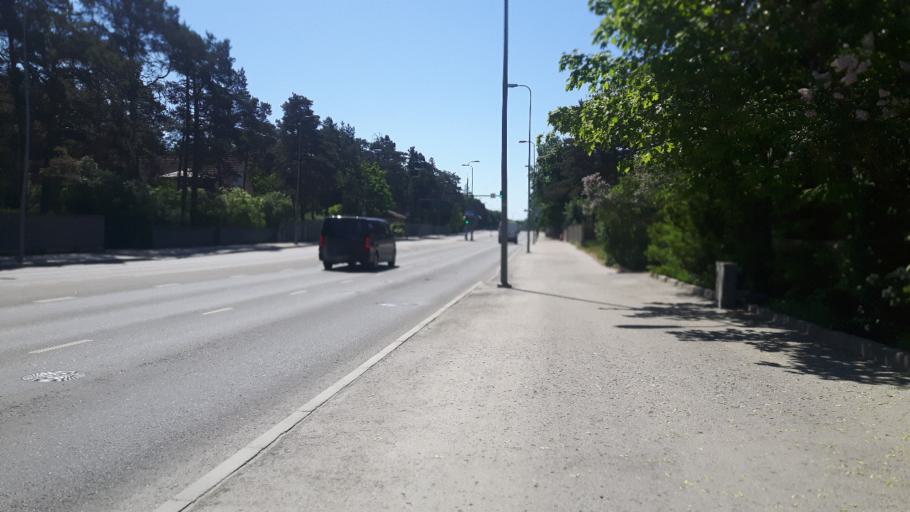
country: EE
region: Harju
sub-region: Tallinna linn
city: Tallinn
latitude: 59.3811
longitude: 24.7174
